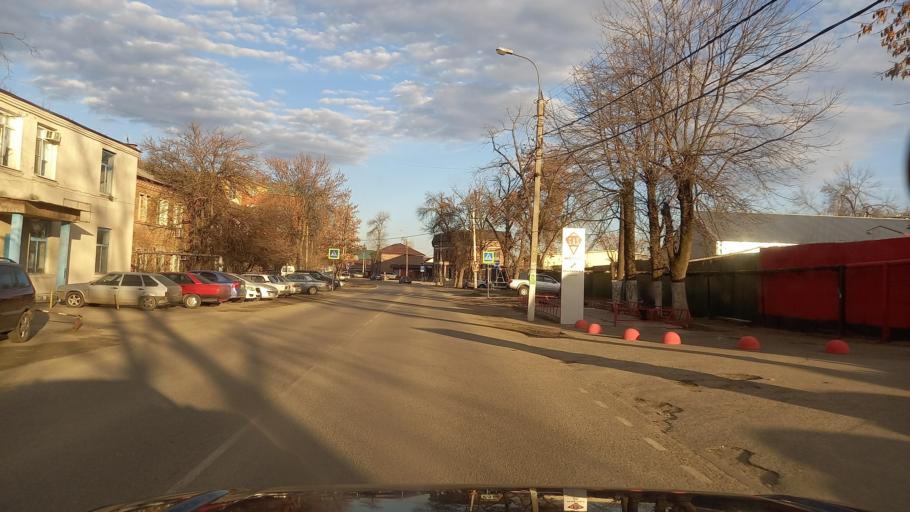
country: RU
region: Krasnodarskiy
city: Pashkovskiy
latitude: 45.0153
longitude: 39.1061
